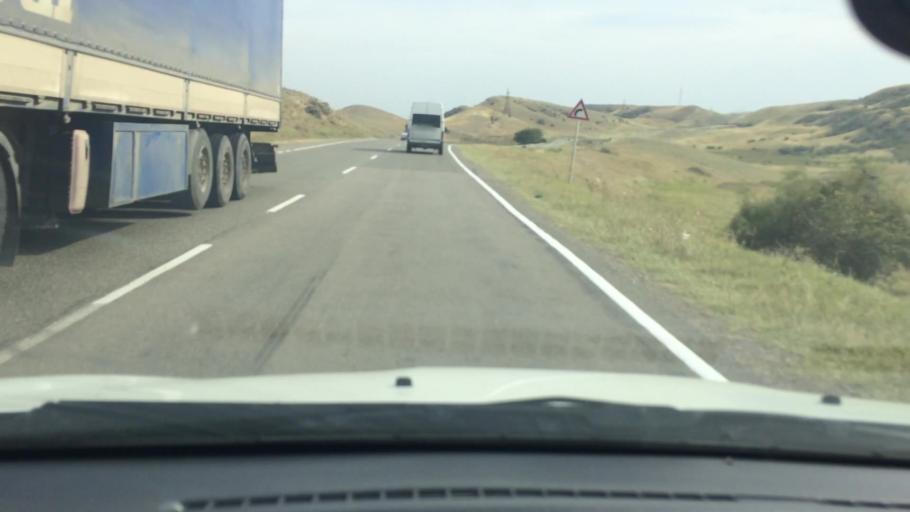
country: GE
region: Kvemo Kartli
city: Rust'avi
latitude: 41.5324
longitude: 44.9832
